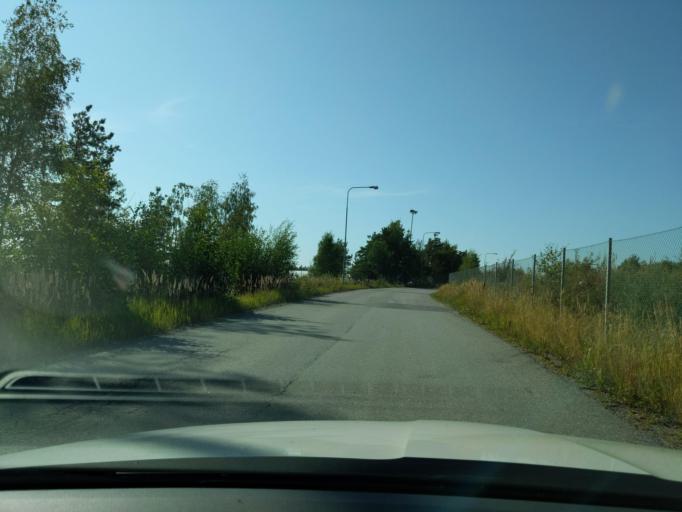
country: FI
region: Uusimaa
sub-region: Raaseporin
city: Inga
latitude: 60.0180
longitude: 23.9250
